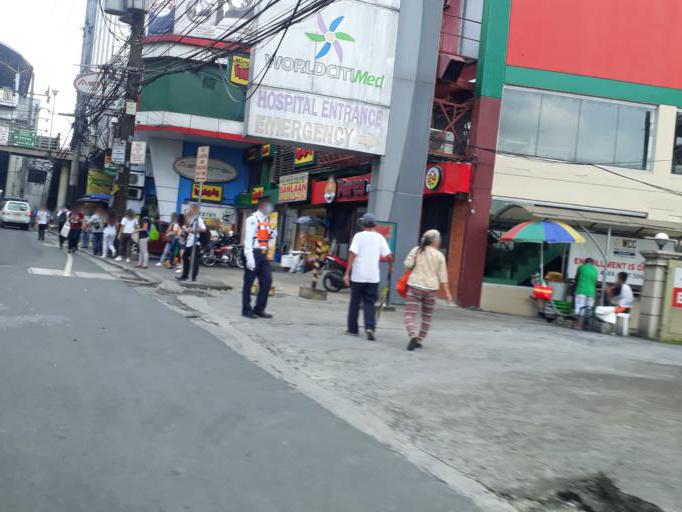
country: PH
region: Metro Manila
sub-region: Quezon City
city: Quezon City
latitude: 14.6277
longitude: 121.0634
